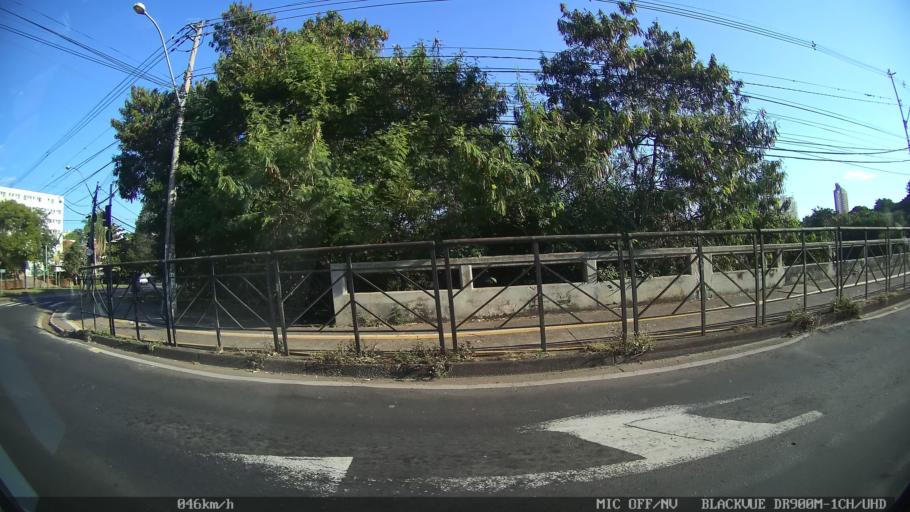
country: BR
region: Sao Paulo
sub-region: Piracicaba
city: Piracicaba
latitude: -22.7148
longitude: -47.6507
